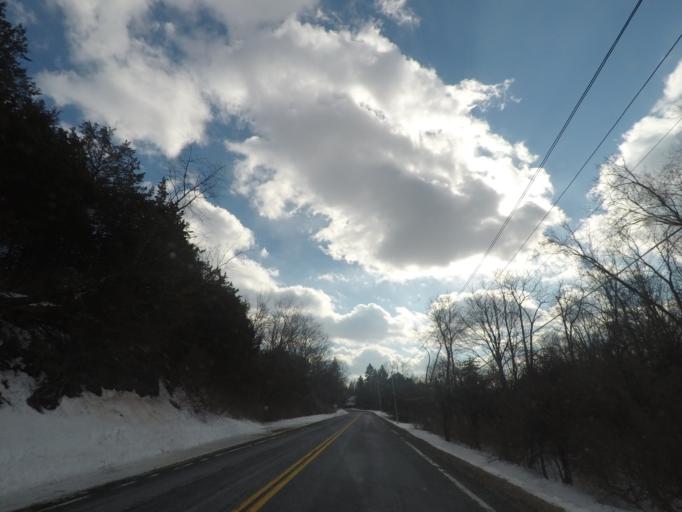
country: US
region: New York
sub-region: Schenectady County
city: Niskayuna
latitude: 42.8174
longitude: -73.8488
